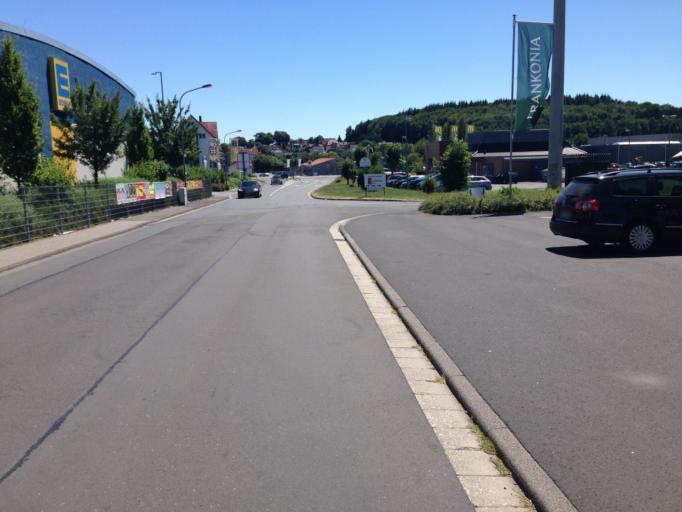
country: DE
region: Hesse
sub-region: Regierungsbezirk Giessen
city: Reiskirchen
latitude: 50.5989
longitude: 8.8221
